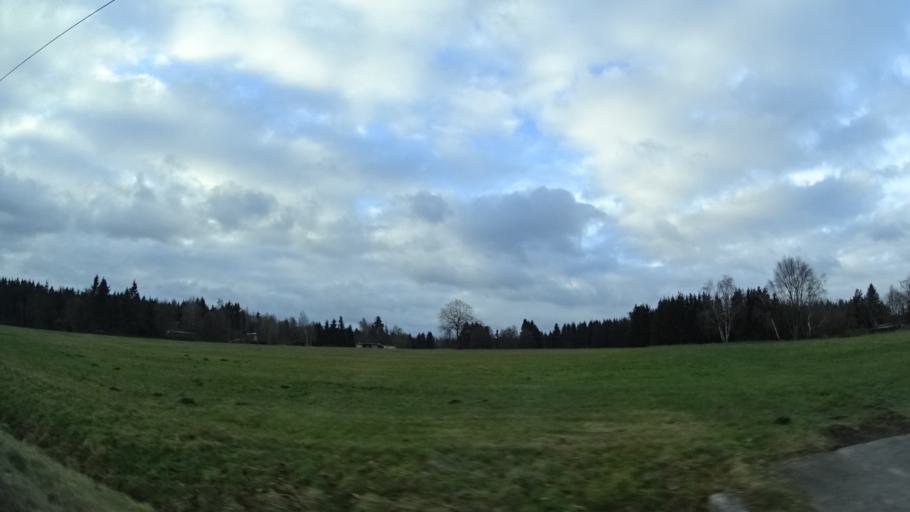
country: DE
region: Thuringia
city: Zeulenroda
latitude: 50.6290
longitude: 11.9968
